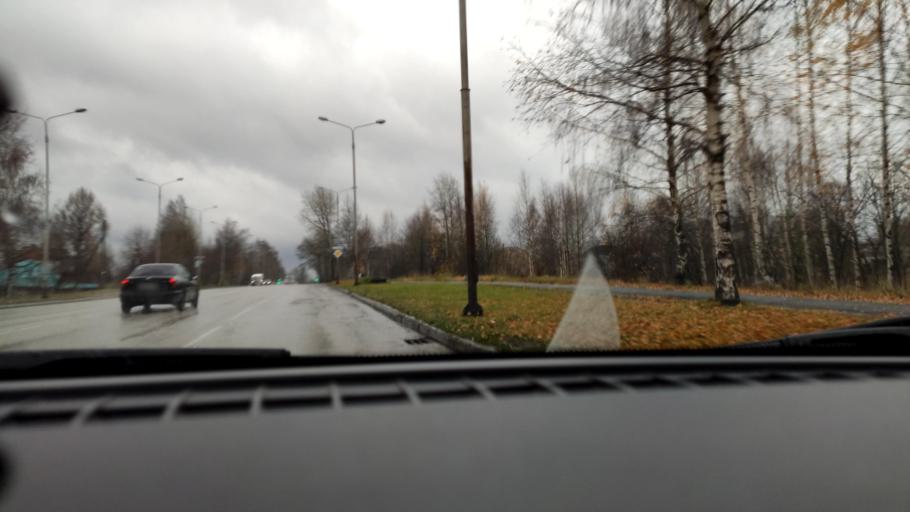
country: RU
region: Perm
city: Perm
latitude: 58.0956
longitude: 56.3844
